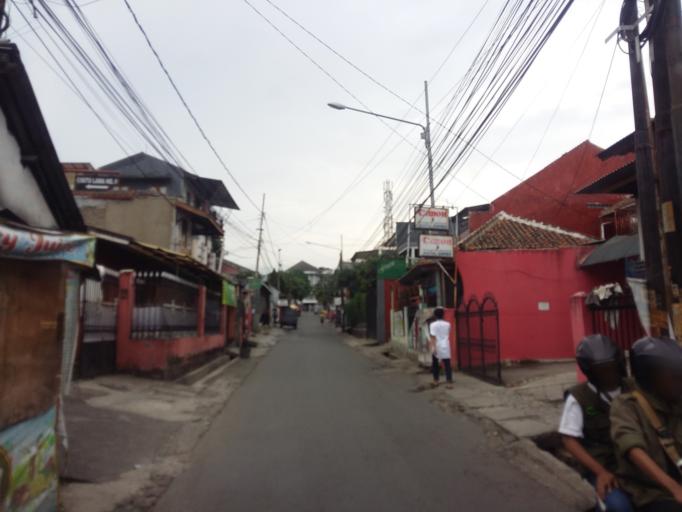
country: ID
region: West Java
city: Bandung
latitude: -6.8813
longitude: 107.6118
